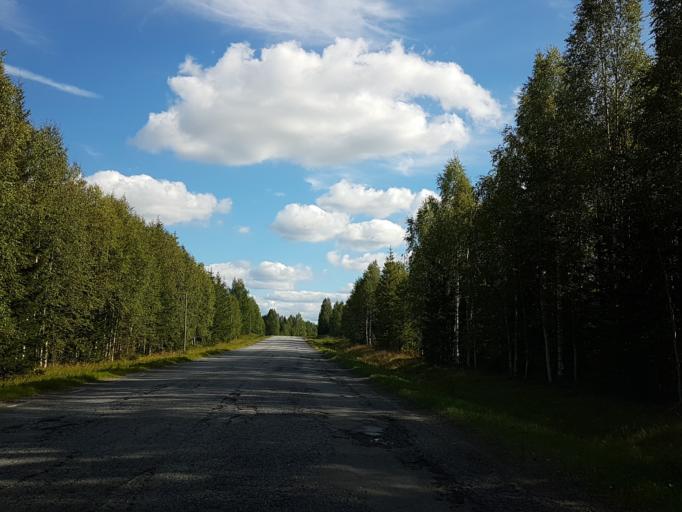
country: SE
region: Vaesterbotten
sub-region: Skelleftea Kommun
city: Burtraesk
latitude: 64.3255
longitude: 20.5283
